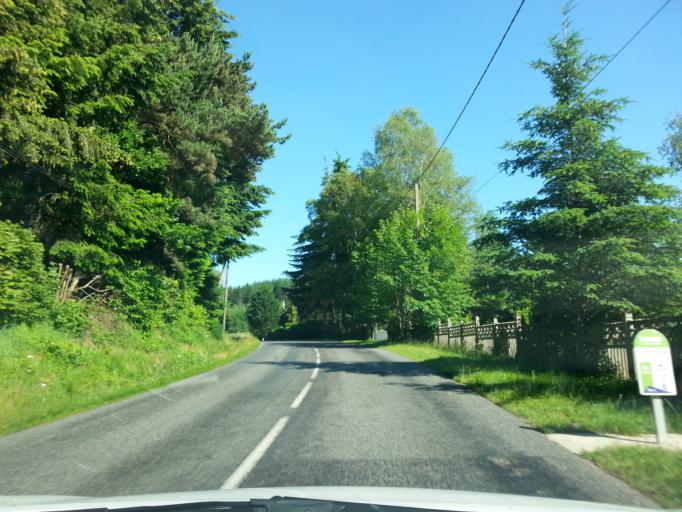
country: FR
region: Rhone-Alpes
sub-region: Departement de la Loire
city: Belmont-de-la-Loire
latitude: 46.1767
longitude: 4.4223
